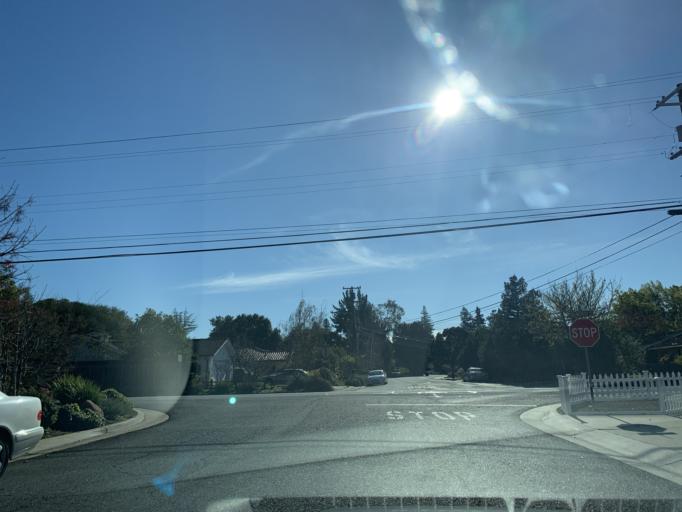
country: US
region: California
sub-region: Santa Clara County
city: Los Altos
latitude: 37.3853
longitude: -122.1045
